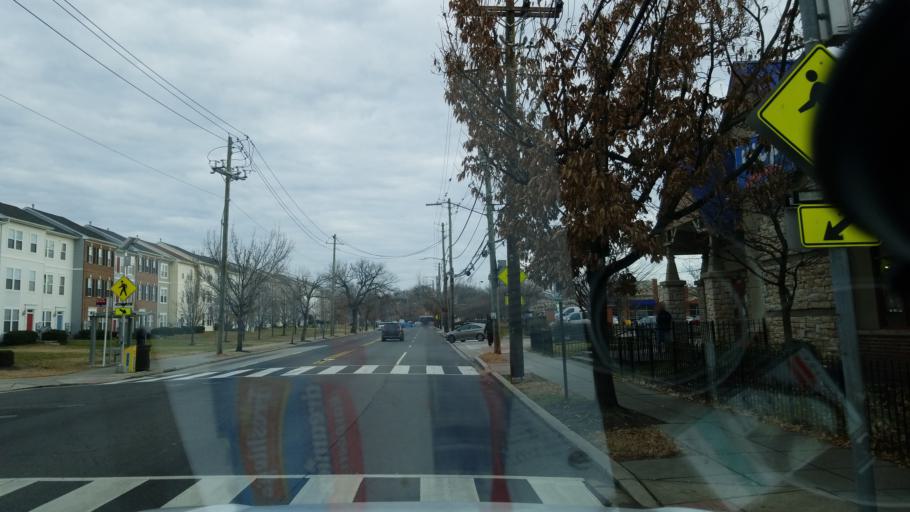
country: US
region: Maryland
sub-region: Prince George's County
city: Hillcrest Heights
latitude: 38.8461
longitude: -76.9830
